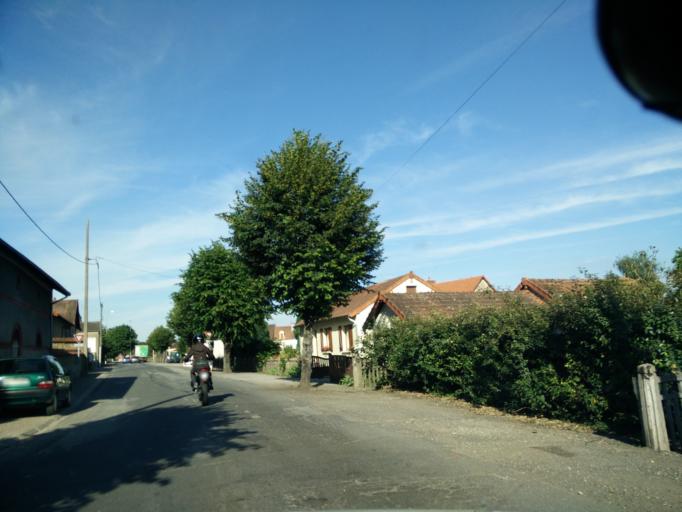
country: FR
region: Auvergne
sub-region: Departement de l'Allier
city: Souvigny
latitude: 46.5316
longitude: 3.1903
